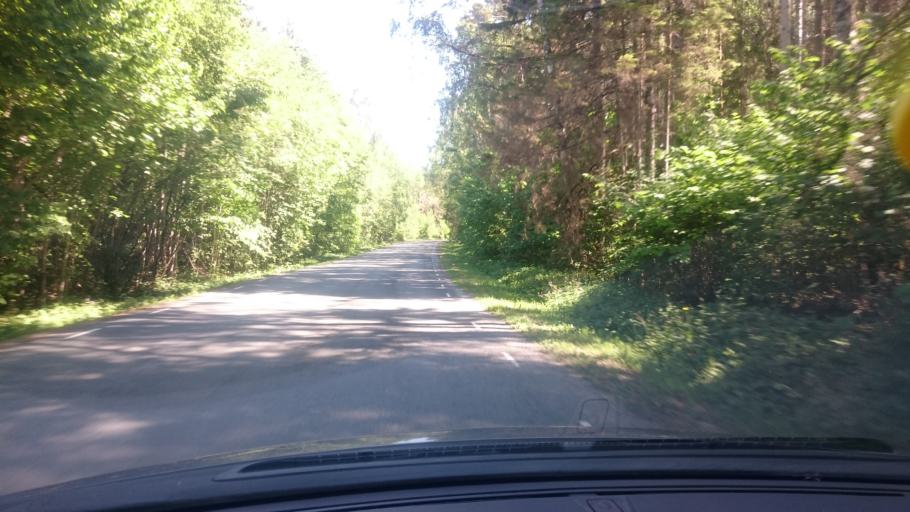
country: EE
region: Harju
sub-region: Rae vald
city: Vaida
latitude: 59.2066
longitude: 24.9338
